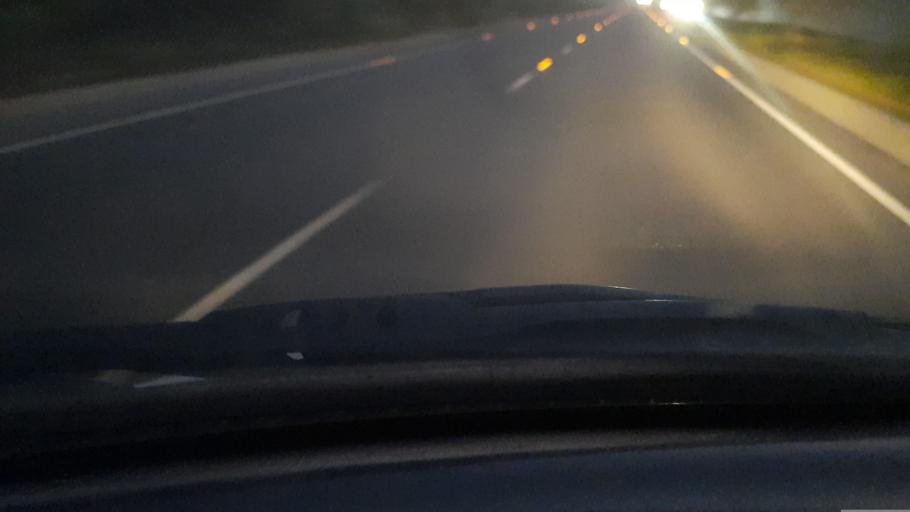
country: BD
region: Dhaka
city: Char Bhadrasan
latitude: 23.4010
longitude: 90.1732
